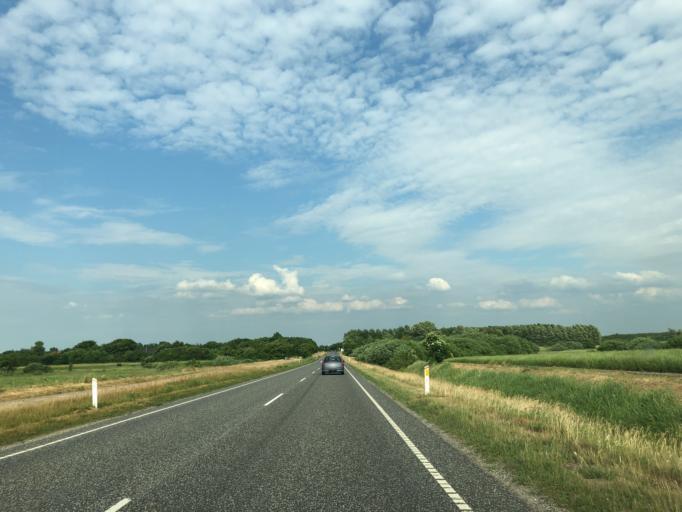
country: DK
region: Central Jutland
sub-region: Ringkobing-Skjern Kommune
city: Tarm
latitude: 55.9020
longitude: 8.4933
